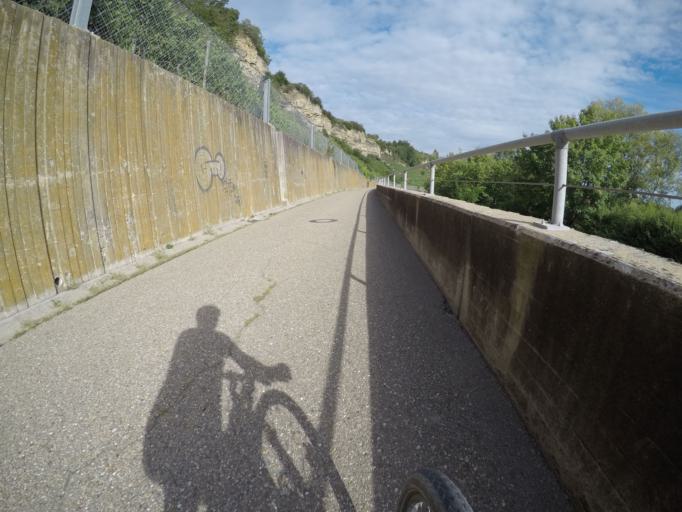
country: DE
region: Baden-Wuerttemberg
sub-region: Regierungsbezirk Stuttgart
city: Marbach am Neckar
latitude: 48.9130
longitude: 9.2523
